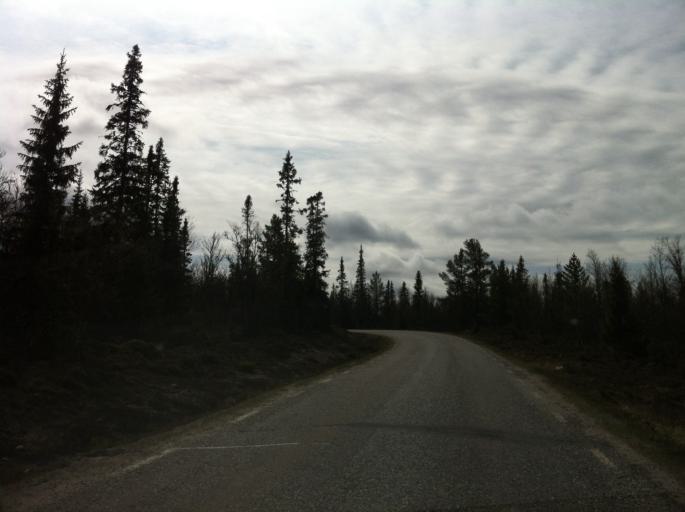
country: NO
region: Hedmark
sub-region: Engerdal
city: Engerdal
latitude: 62.3093
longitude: 12.8084
